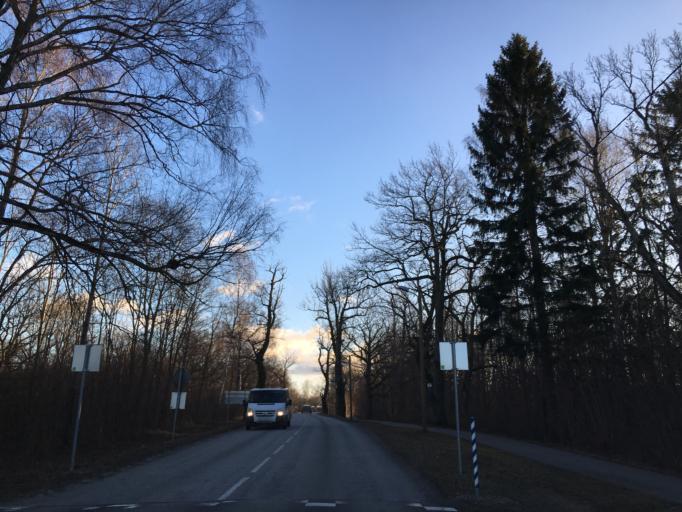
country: EE
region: Harju
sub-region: Saue linn
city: Saue
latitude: 59.3189
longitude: 24.5542
